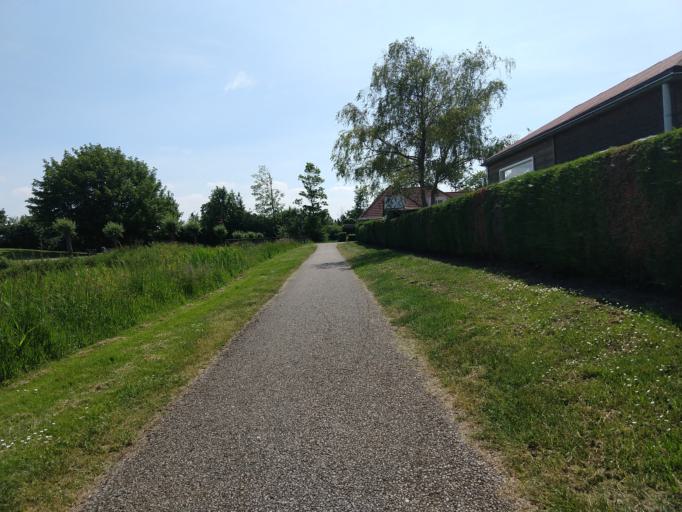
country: NL
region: Zeeland
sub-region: Gemeente Borsele
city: Borssele
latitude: 51.4566
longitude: 3.7724
